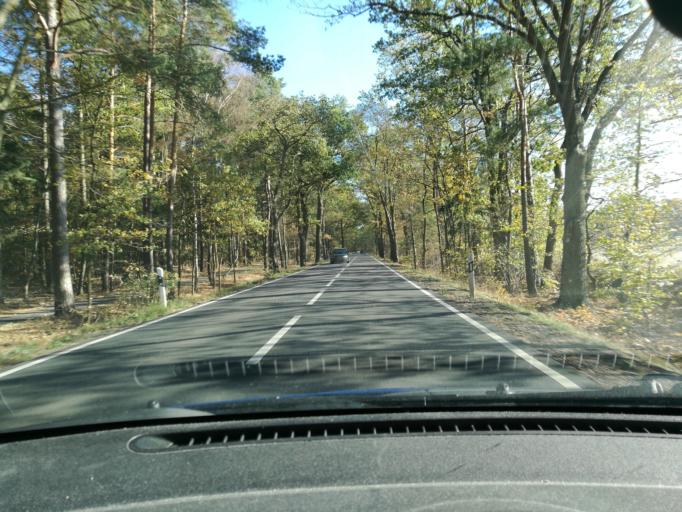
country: DE
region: Lower Saxony
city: Damnatz
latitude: 53.1024
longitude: 11.1540
